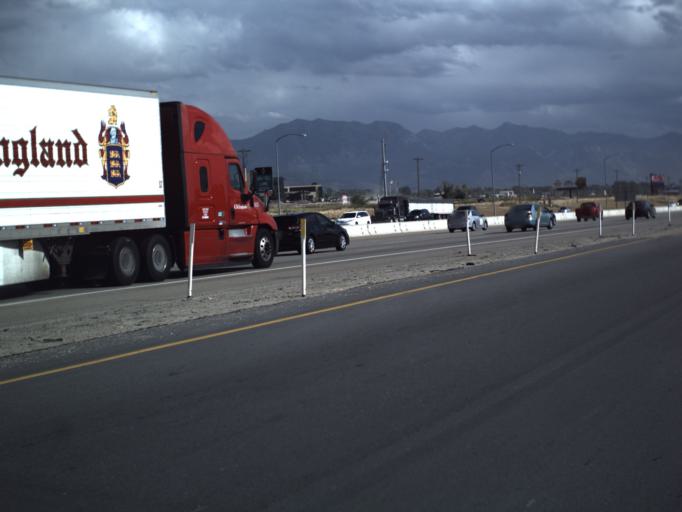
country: US
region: Utah
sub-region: Utah County
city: Lehi
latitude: 40.4289
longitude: -111.8888
